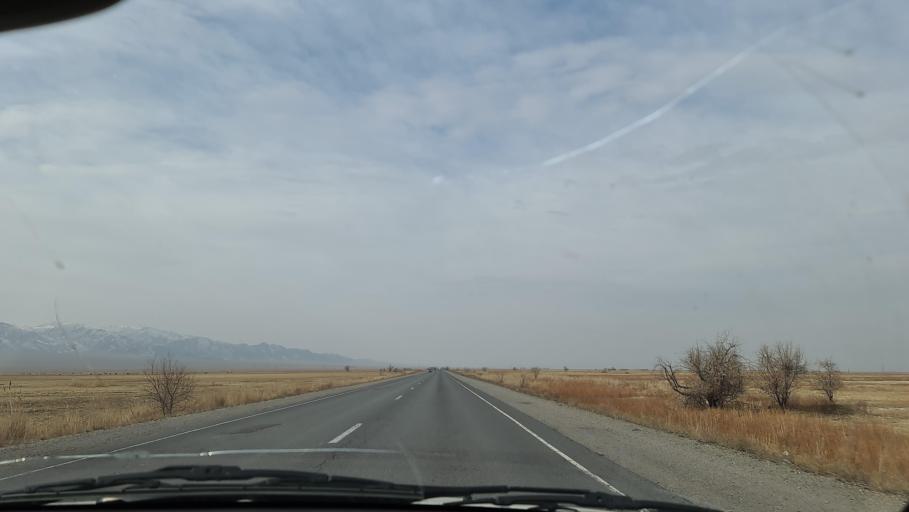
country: KG
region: Chuy
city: Tokmok
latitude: 43.3540
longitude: 75.4435
